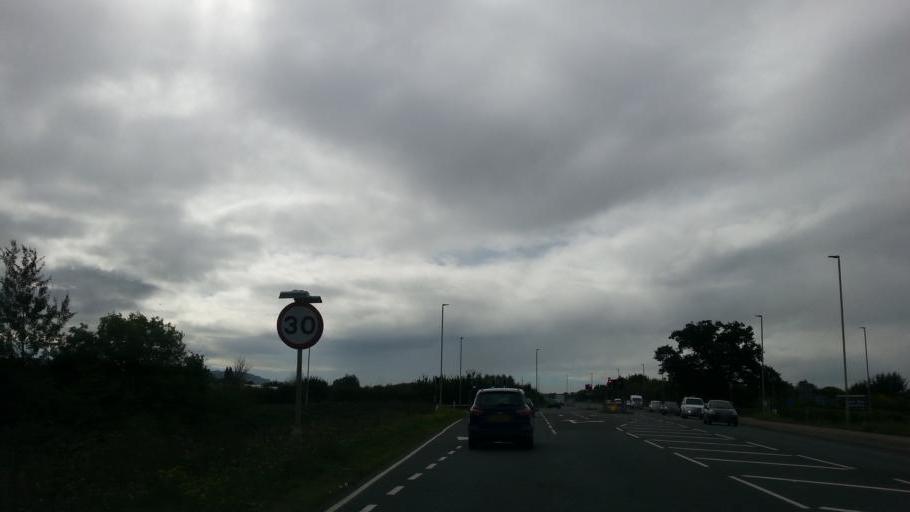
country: GB
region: England
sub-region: Gloucestershire
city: Gloucester
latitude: 51.8429
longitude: -2.2710
